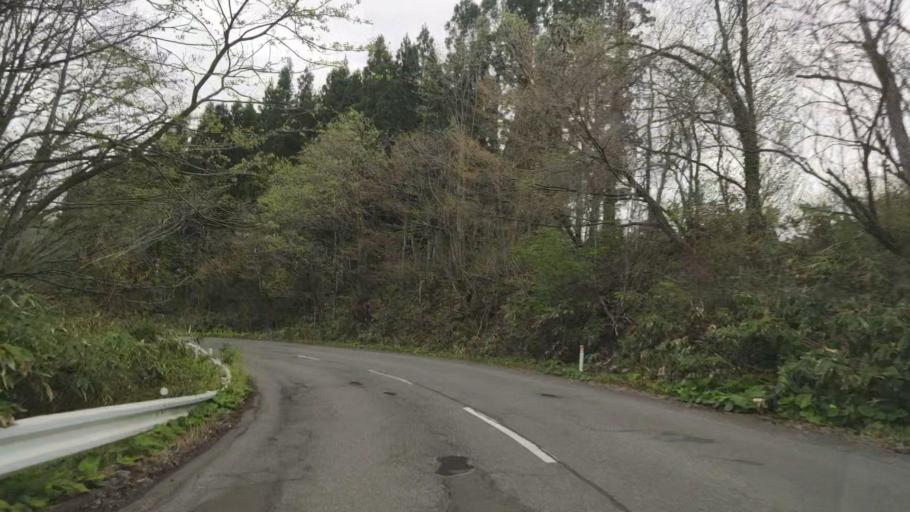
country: JP
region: Akita
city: Hanawa
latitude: 40.3760
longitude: 140.7894
